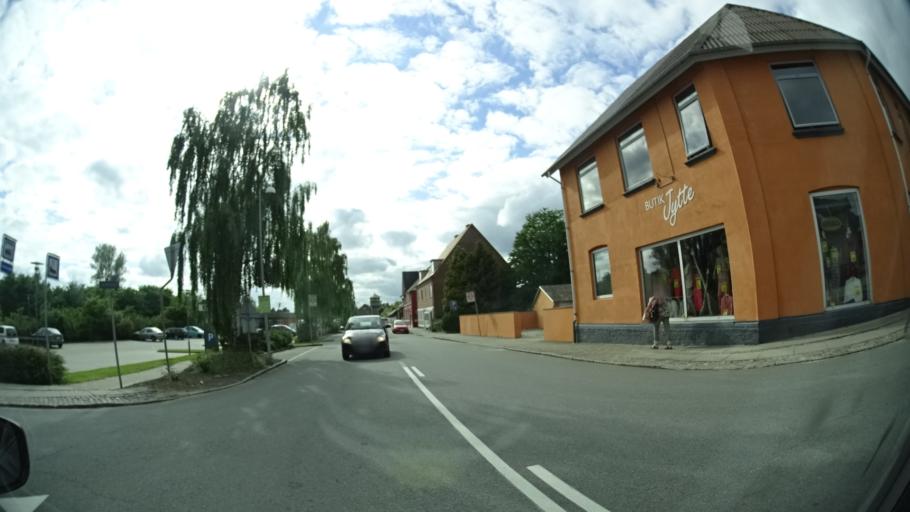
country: DK
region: Central Jutland
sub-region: Syddjurs Kommune
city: Ryomgard
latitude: 56.3800
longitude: 10.5042
